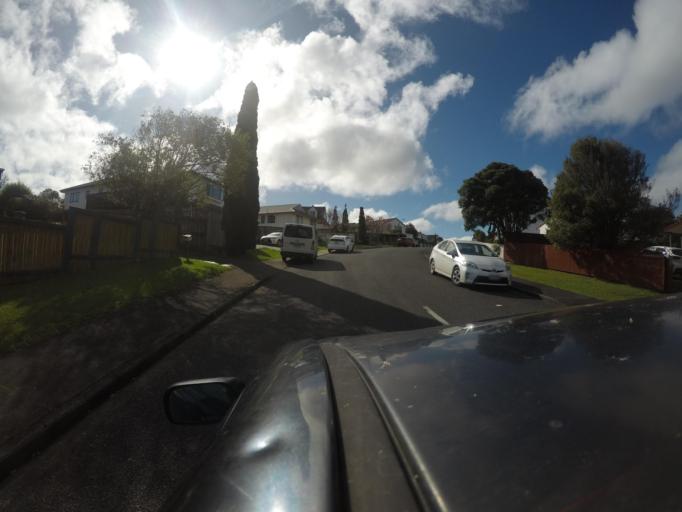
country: NZ
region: Auckland
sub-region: Auckland
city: Waitakere
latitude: -36.8949
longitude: 174.6559
